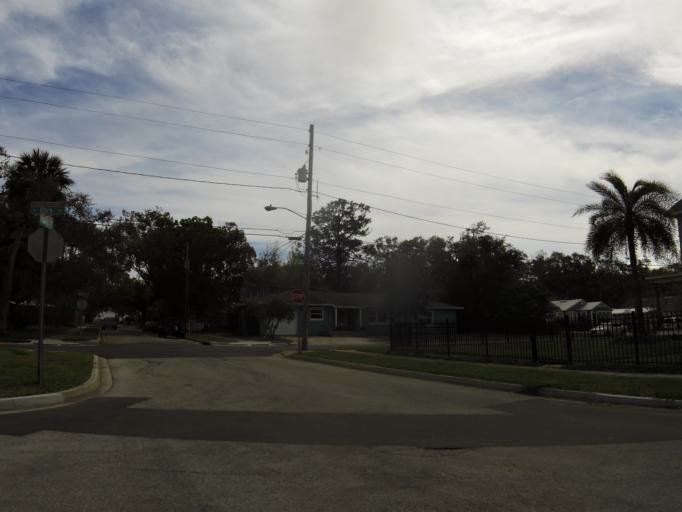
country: US
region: Florida
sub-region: Saint Johns County
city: Saint Augustine
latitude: 29.9167
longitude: -81.3168
